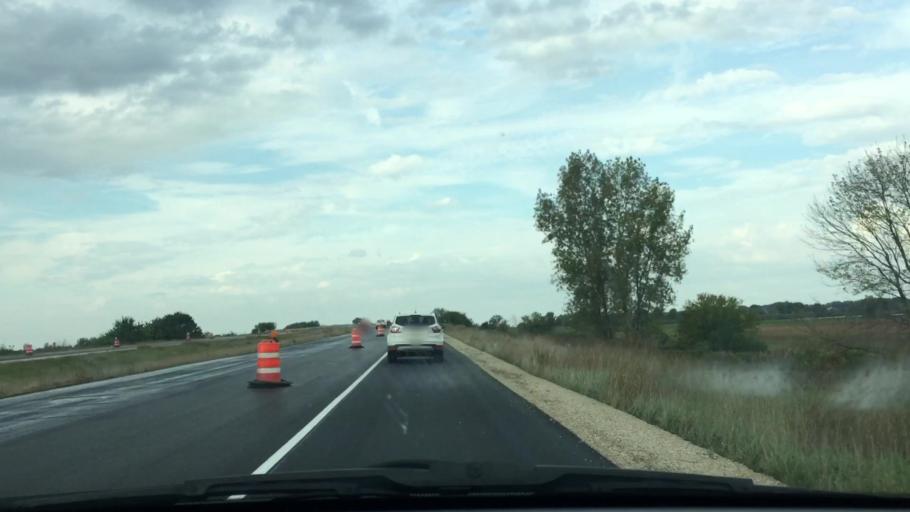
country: US
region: Illinois
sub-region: Whiteside County
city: Prophetstown
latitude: 41.7161
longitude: -89.9942
